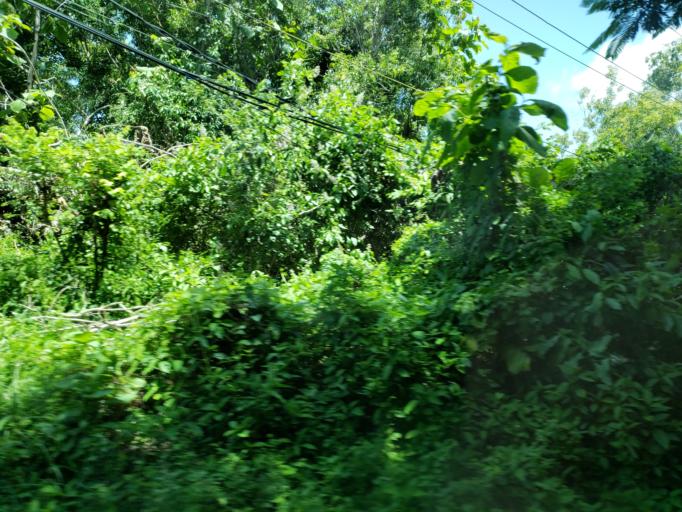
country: ID
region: Bali
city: Kangin
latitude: -8.8329
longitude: 115.1354
